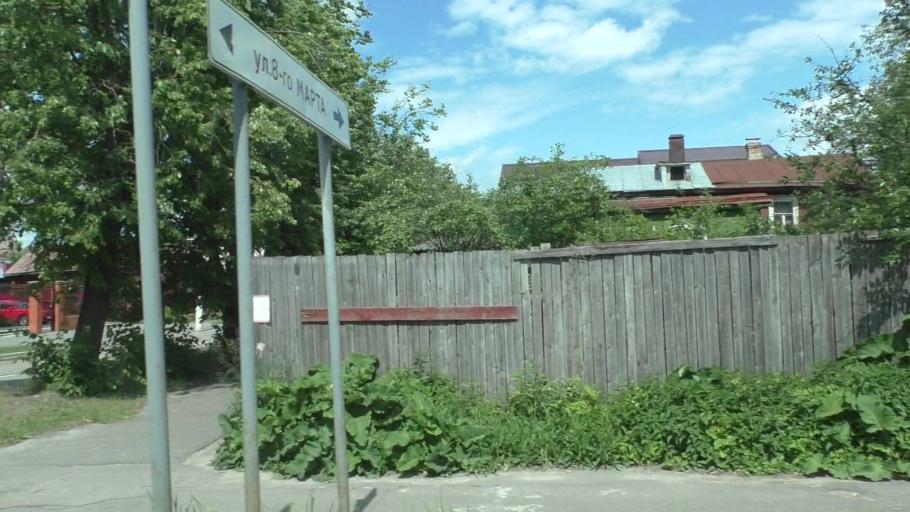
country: RU
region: Moskovskaya
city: Yegor'yevsk
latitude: 55.3829
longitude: 39.0397
